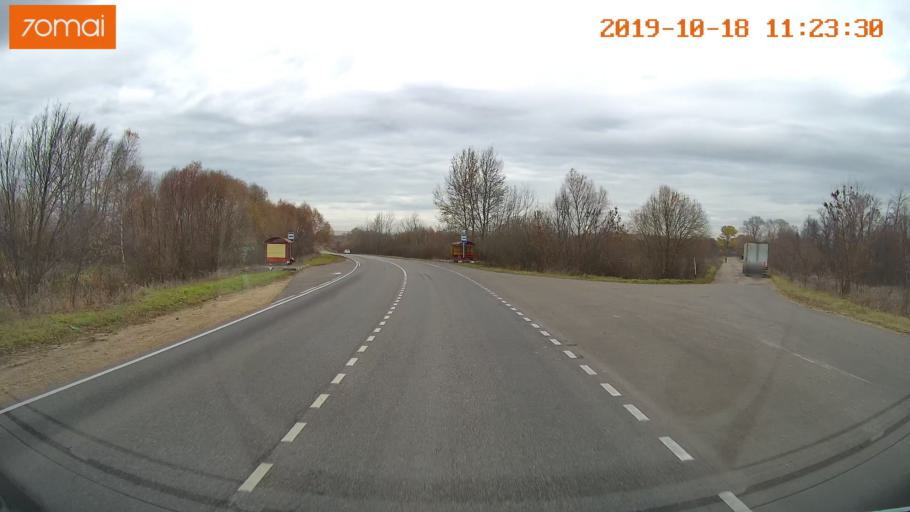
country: RU
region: Tula
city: Kimovsk
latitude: 54.1024
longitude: 38.5948
